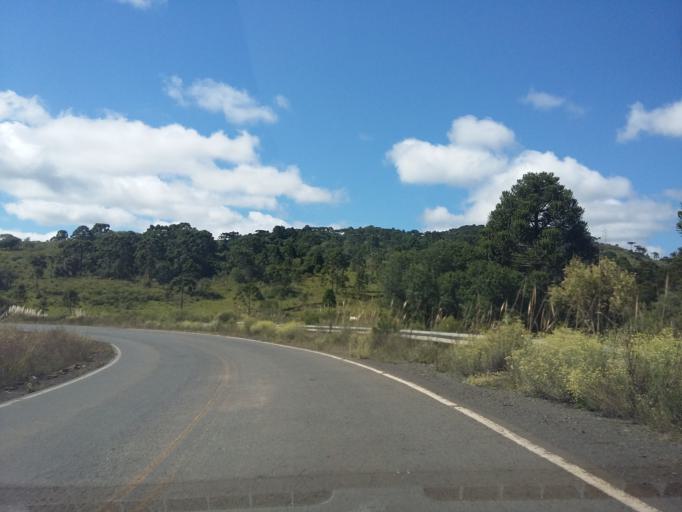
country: BR
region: Santa Catarina
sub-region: Sao Joaquim
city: Sao Joaquim
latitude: -28.0913
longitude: -50.0607
